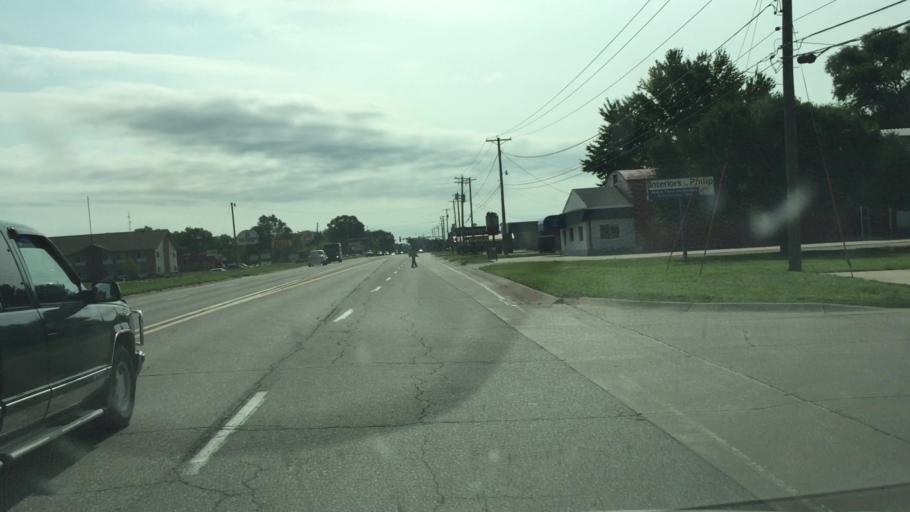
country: US
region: Iowa
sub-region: Lee County
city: Fort Madison
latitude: 40.6240
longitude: -91.3772
